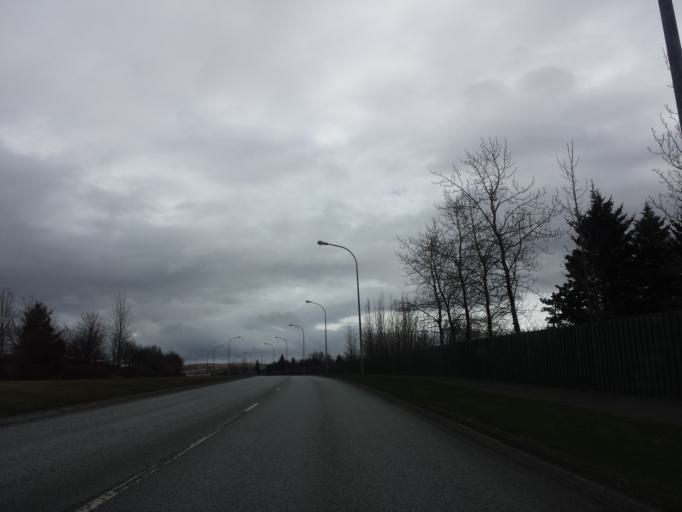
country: IS
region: Capital Region
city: Gardabaer
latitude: 64.0861
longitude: -21.9149
